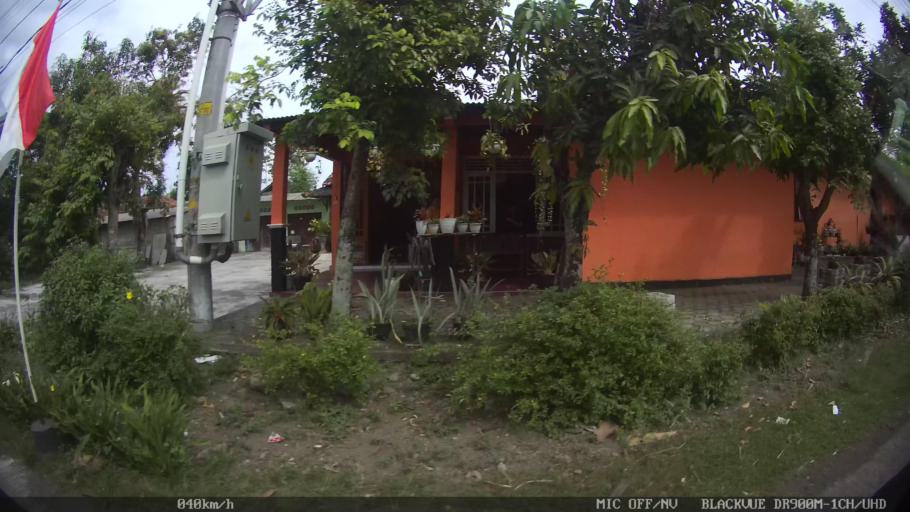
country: ID
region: Daerah Istimewa Yogyakarta
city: Depok
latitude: -7.8150
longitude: 110.4429
